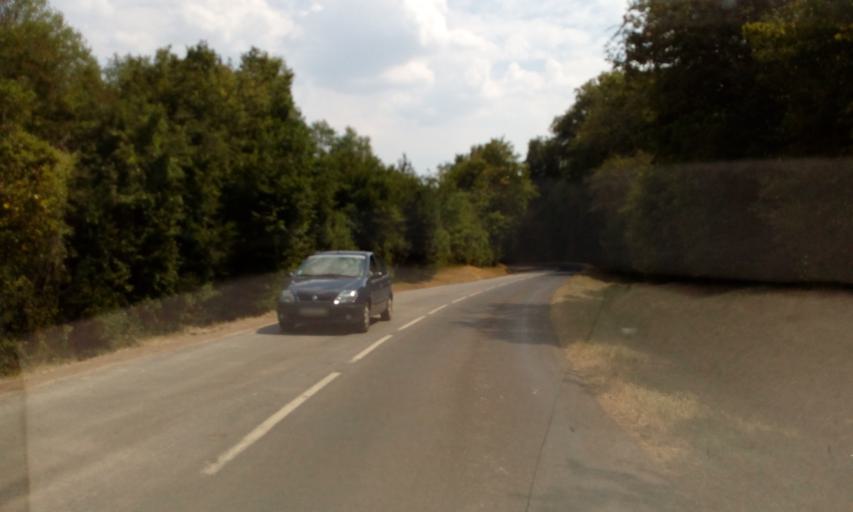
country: FR
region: Lorraine
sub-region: Departement de Meurthe-et-Moselle
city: Pagny-sur-Moselle
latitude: 48.9693
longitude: 5.8774
